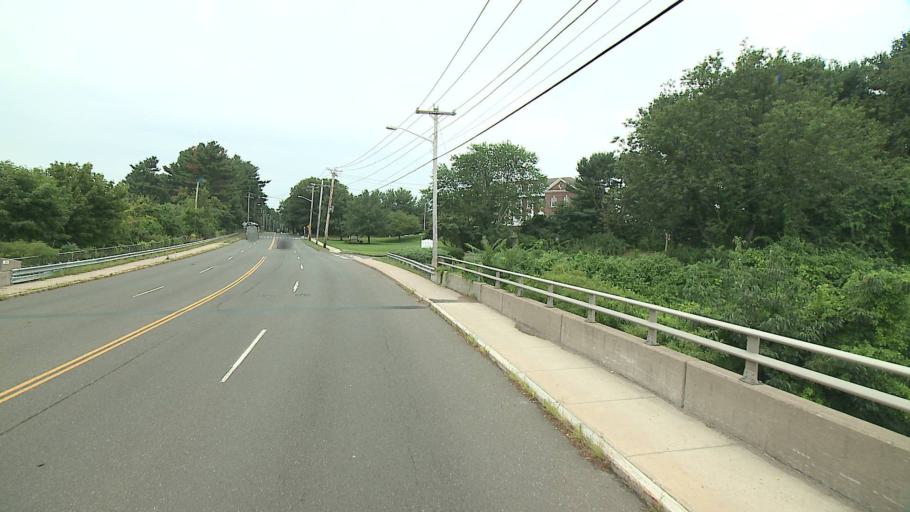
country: US
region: Connecticut
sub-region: New Haven County
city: Hamden
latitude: 41.3543
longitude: -72.9132
